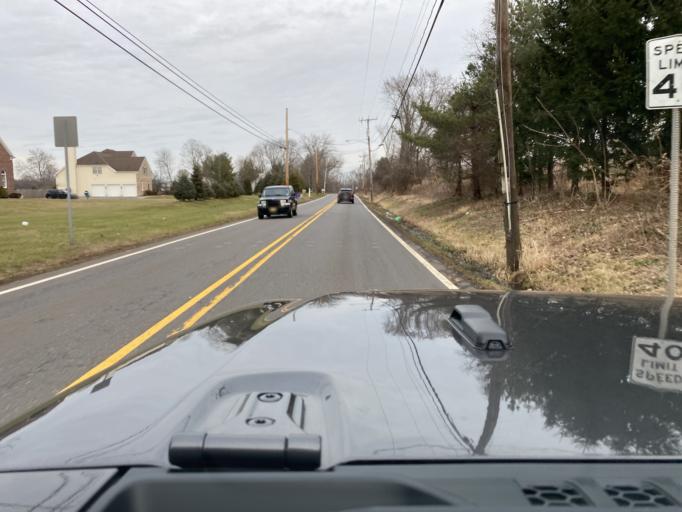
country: US
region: New Jersey
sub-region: Somerset County
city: Bloomingdale
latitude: 40.5006
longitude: -74.7101
